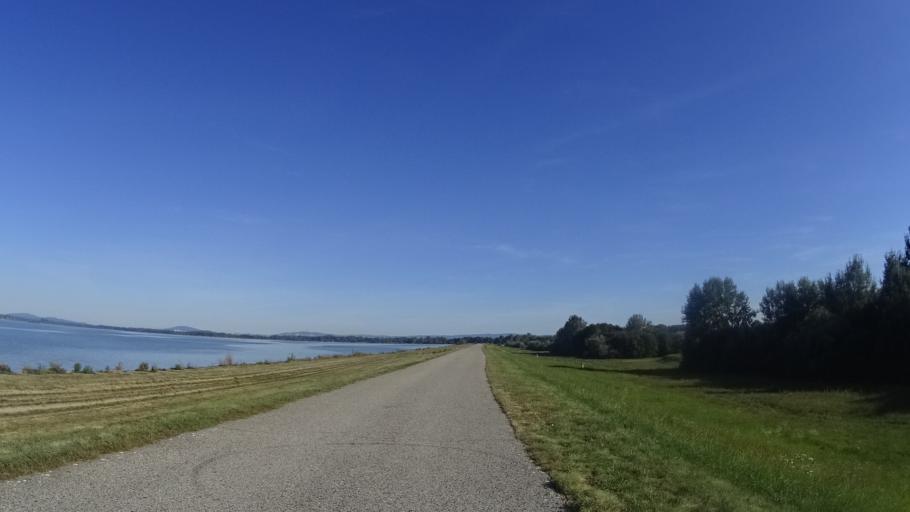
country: SK
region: Bratislavsky
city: Dunajska Luzna
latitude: 48.0368
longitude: 17.2433
